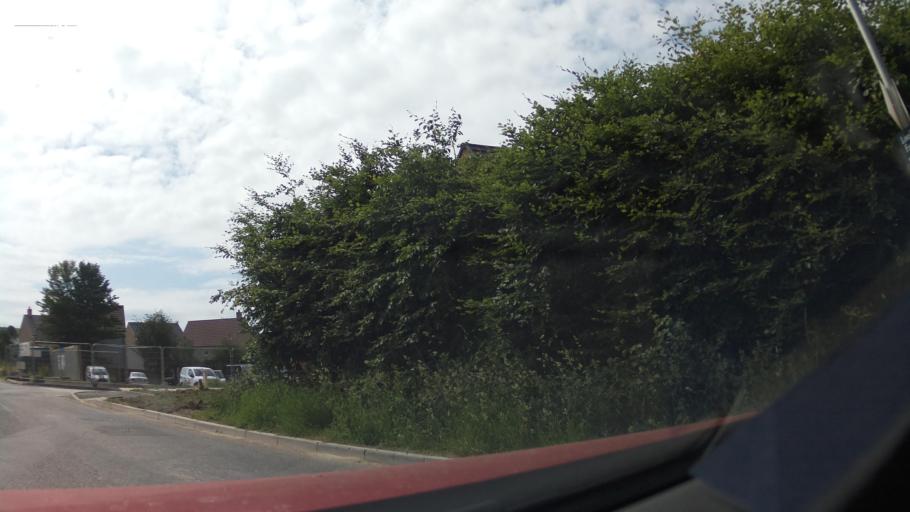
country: GB
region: England
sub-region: Somerset
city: Castle Cary
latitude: 51.0951
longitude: -2.5241
